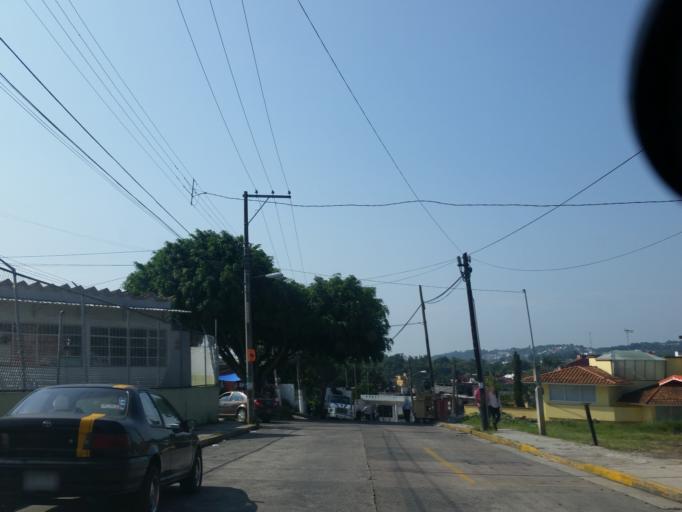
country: MX
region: Veracruz
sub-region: Xalapa
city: Xalapa de Enriquez
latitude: 19.5242
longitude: -96.9035
